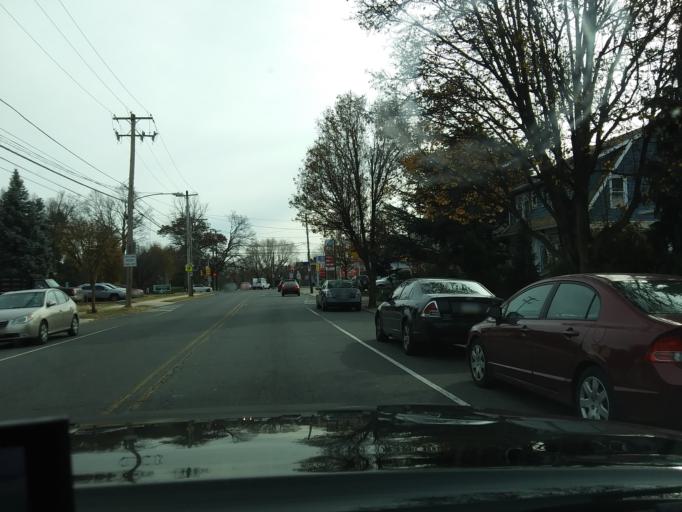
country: US
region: Pennsylvania
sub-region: Montgomery County
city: Rockledge
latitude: 40.0735
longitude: -75.0769
